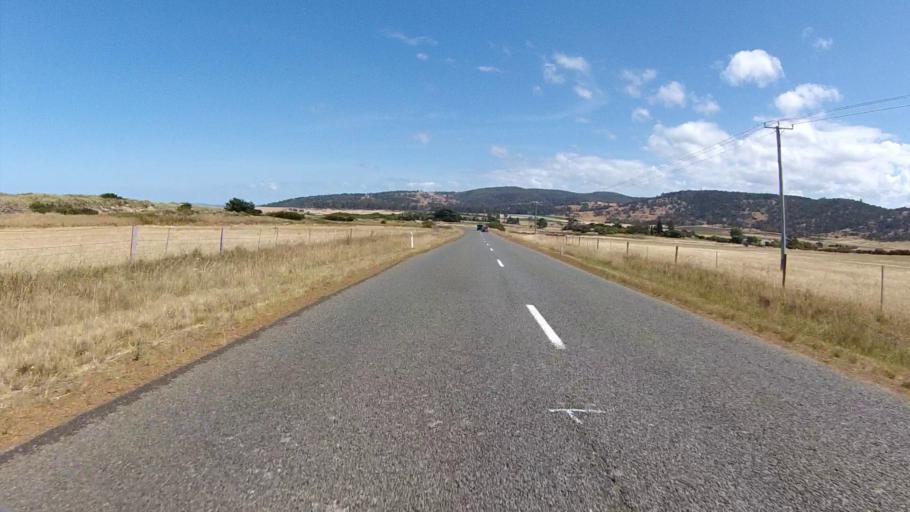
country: AU
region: Tasmania
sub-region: Sorell
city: Sorell
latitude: -42.1963
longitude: 148.0525
